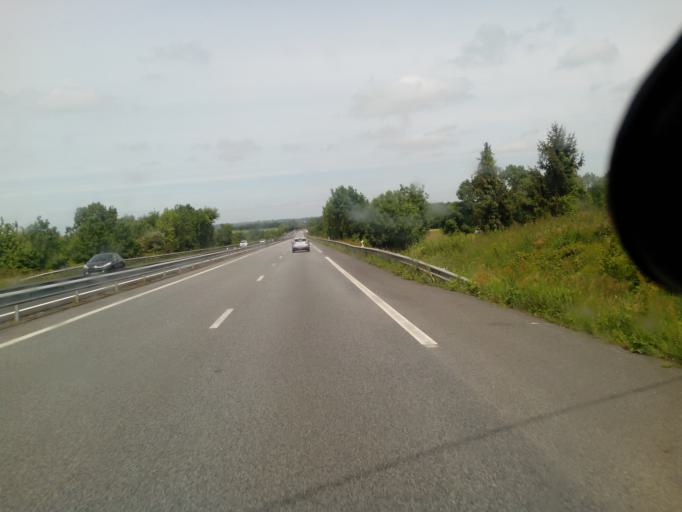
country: FR
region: Pays de la Loire
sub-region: Departement de la Loire-Atlantique
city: Derval
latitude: 47.6794
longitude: -1.6938
